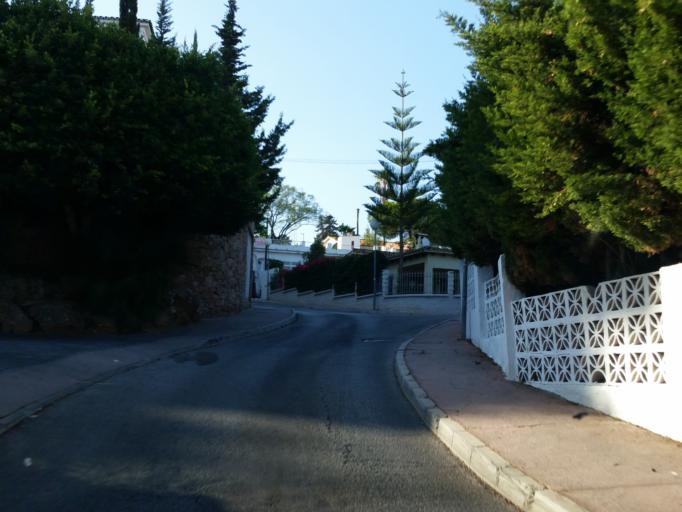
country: ES
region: Andalusia
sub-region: Provincia de Malaga
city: Fuengirola
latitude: 36.5658
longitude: -4.6056
